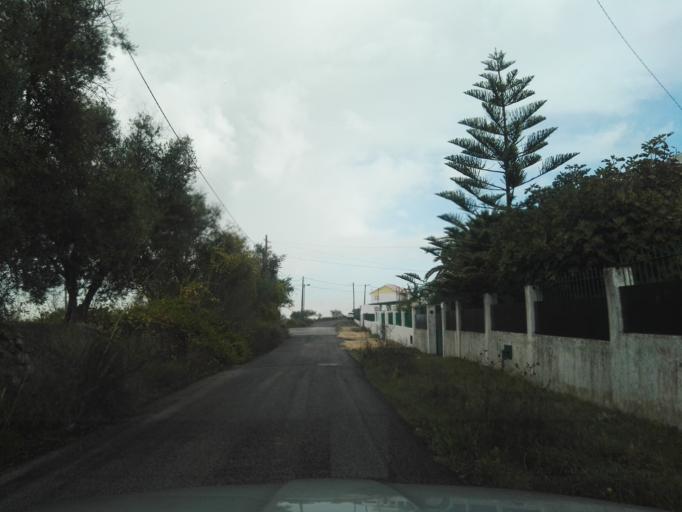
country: PT
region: Lisbon
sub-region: Vila Franca de Xira
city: Vila Franca de Xira
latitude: 38.9710
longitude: -9.0163
